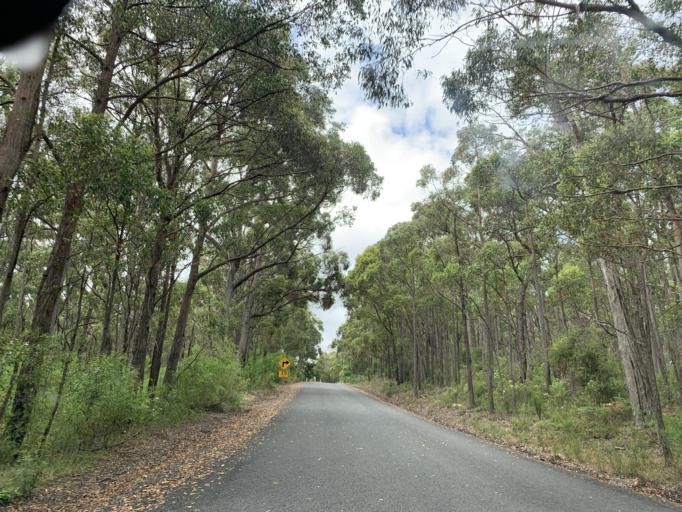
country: AU
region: Victoria
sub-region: Latrobe
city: Traralgon
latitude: -38.1019
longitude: 146.5365
